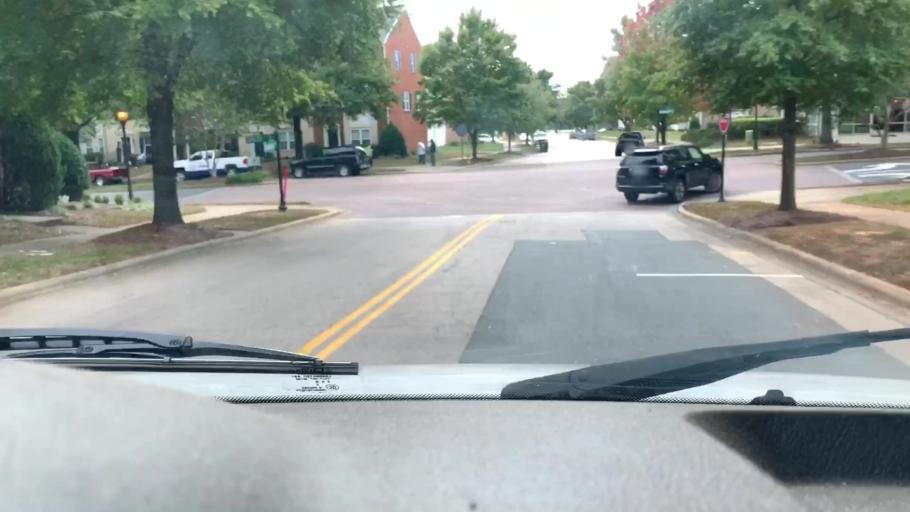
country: US
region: North Carolina
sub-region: Mecklenburg County
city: Cornelius
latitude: 35.4588
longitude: -80.8674
